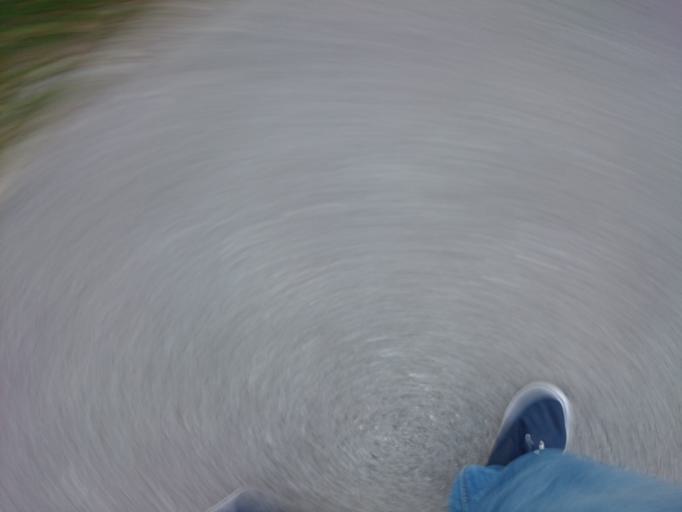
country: HR
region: Licko-Senjska
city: Jezerce
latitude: 44.9708
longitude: 15.6469
